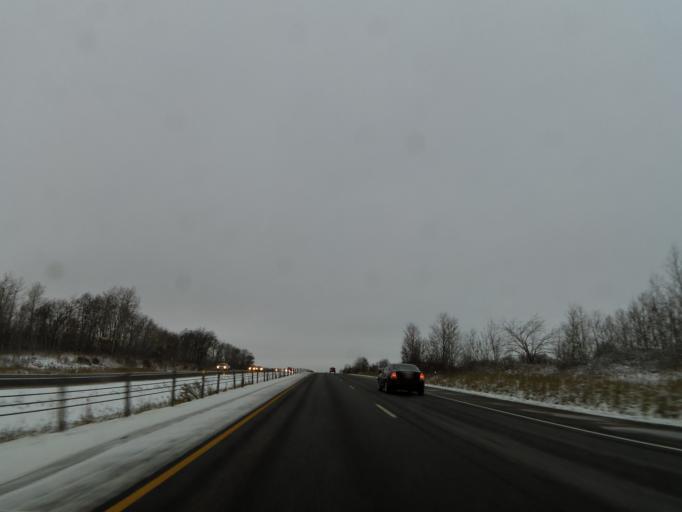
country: US
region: Wisconsin
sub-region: Saint Croix County
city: Hammond
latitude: 44.9407
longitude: -92.4146
